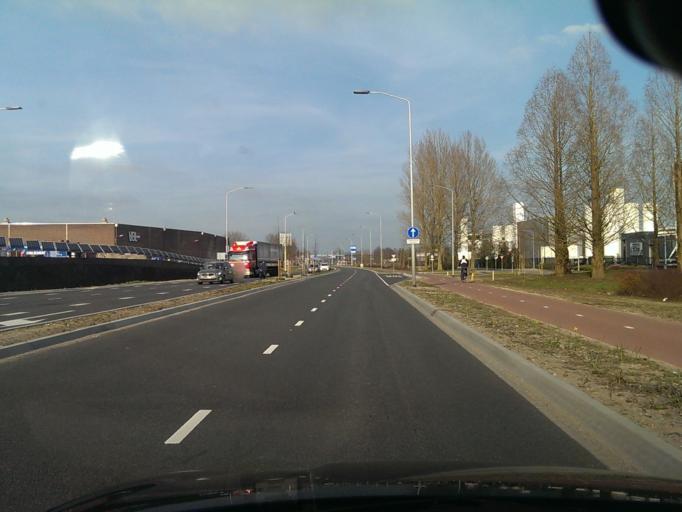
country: NL
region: North Brabant
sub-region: Gemeente Veldhoven
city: Veldhoven
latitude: 51.4046
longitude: 5.4098
